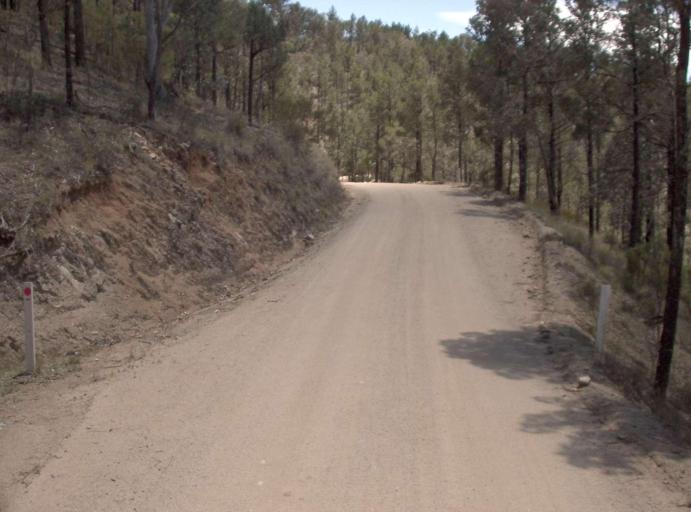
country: AU
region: New South Wales
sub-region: Snowy River
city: Jindabyne
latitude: -36.9078
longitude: 148.4160
